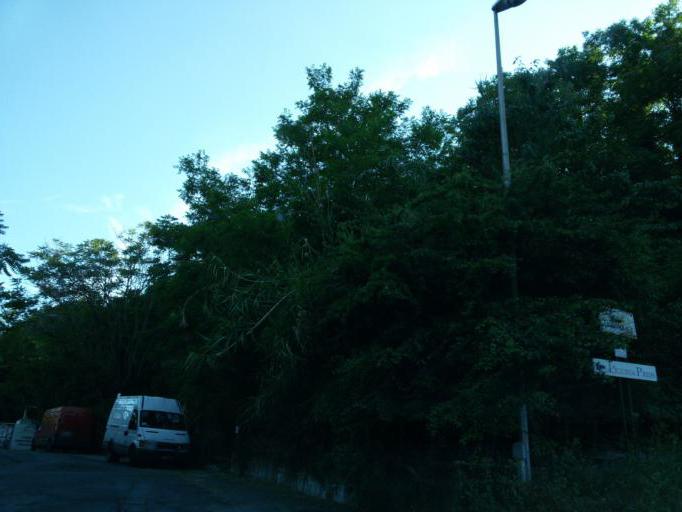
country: IT
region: Liguria
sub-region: Provincia di Genova
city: Manesseno
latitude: 44.4690
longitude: 8.8962
